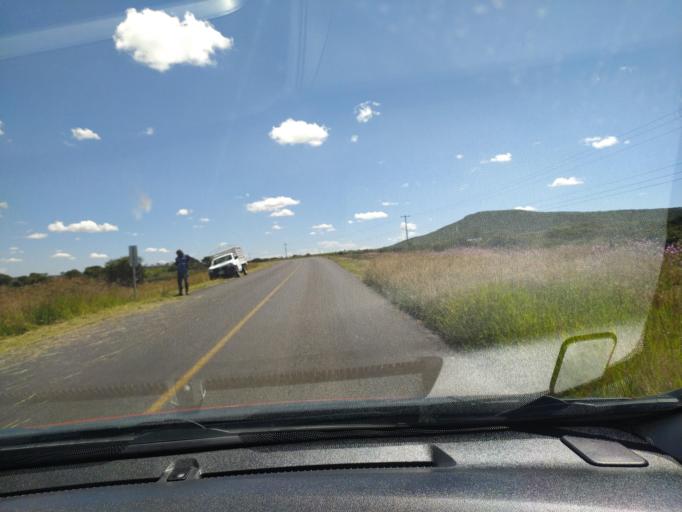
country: MX
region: Jalisco
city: San Miguel el Alto
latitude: 21.0161
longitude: -102.4754
